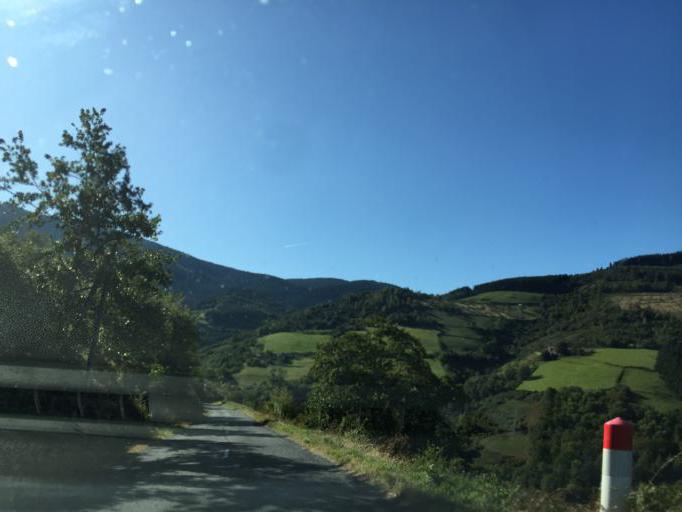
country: FR
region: Rhone-Alpes
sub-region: Departement de la Loire
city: Saint-Chamond
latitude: 45.4070
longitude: 4.5428
